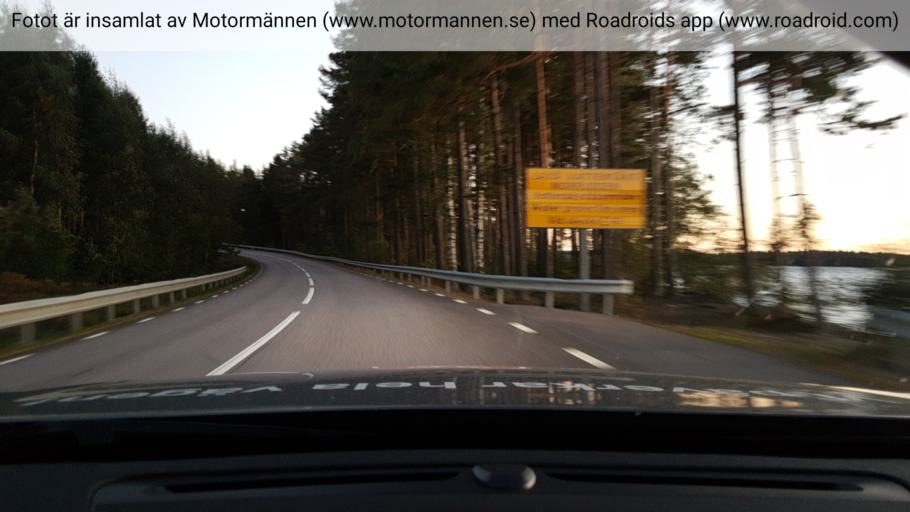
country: SE
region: OErebro
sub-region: Laxa Kommun
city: Laxa
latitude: 58.9022
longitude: 14.7204
